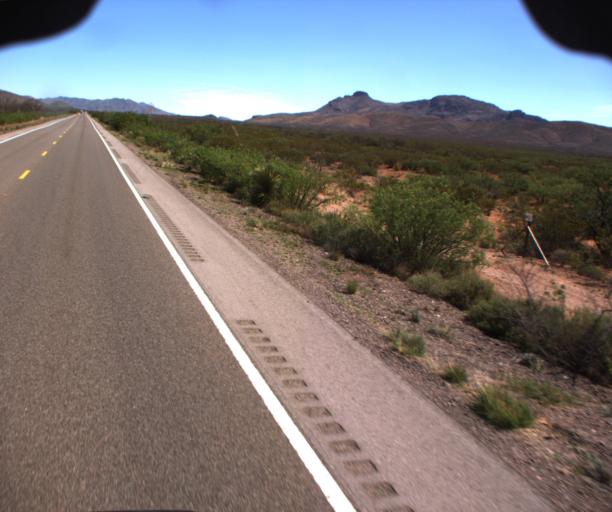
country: US
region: Arizona
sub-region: Cochise County
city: Douglas
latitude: 31.4285
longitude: -109.4850
